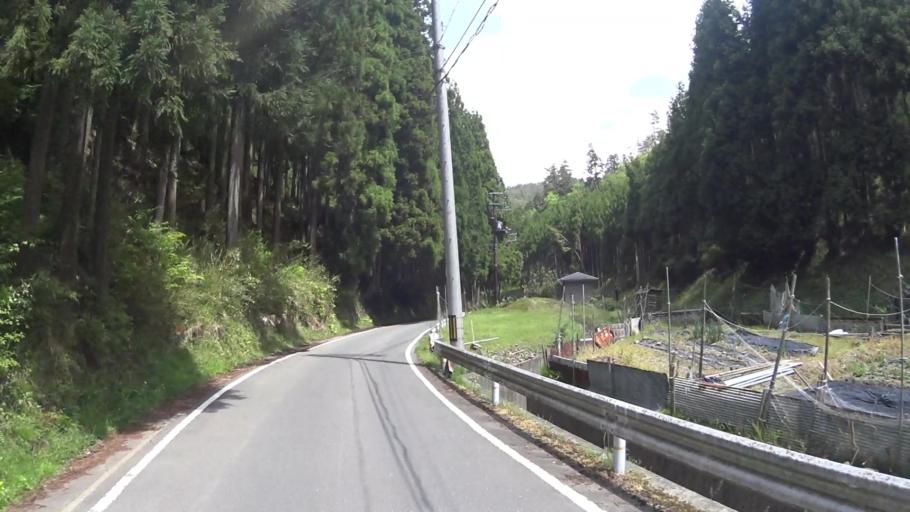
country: JP
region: Kyoto
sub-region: Kyoto-shi
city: Kamigyo-ku
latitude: 35.0755
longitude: 135.7129
